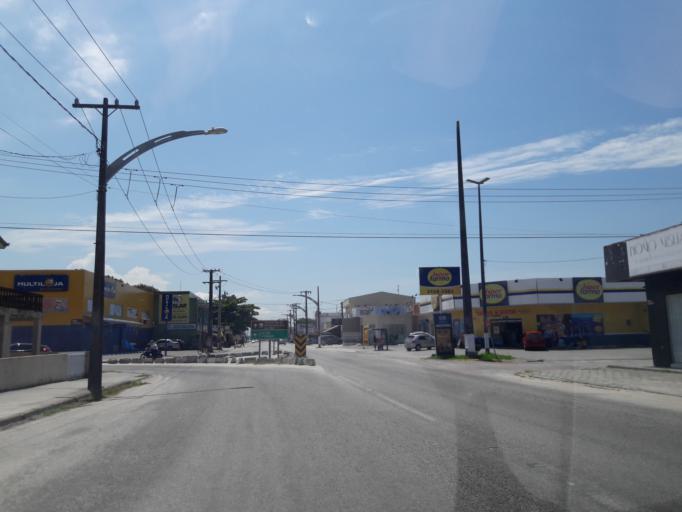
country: BR
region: Parana
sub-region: Pontal Do Parana
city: Pontal do Parana
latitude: -25.6966
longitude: -48.4756
